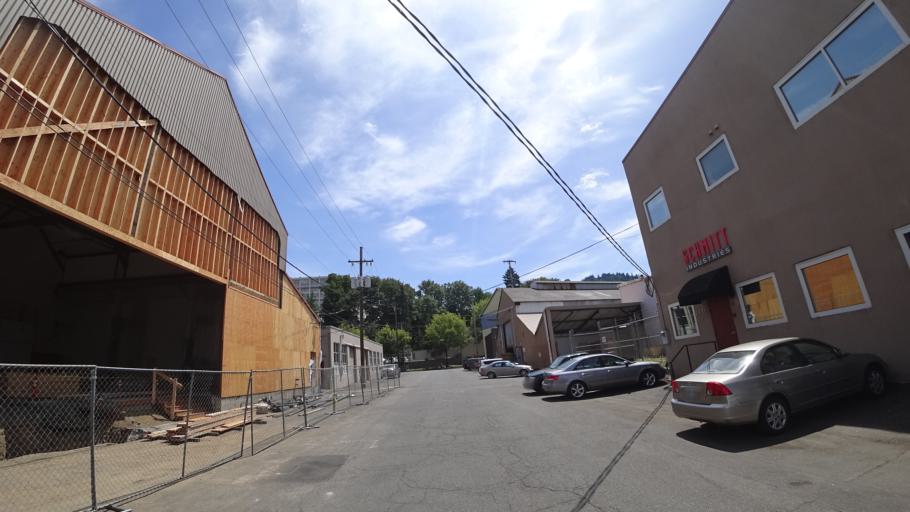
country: US
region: Oregon
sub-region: Multnomah County
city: Portland
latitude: 45.5399
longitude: -122.7091
